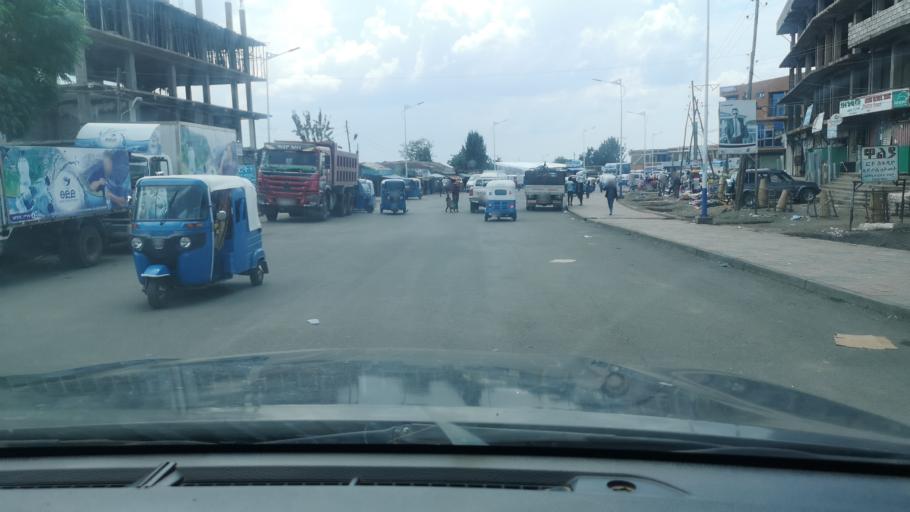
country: ET
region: Oromiya
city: Waliso
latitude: 8.2833
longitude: 37.7797
